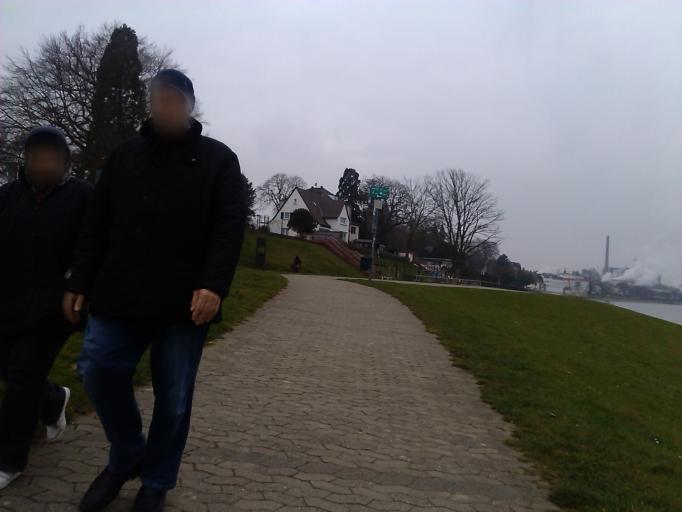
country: DE
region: North Rhine-Westphalia
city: Wesseling
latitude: 50.8243
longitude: 6.9885
